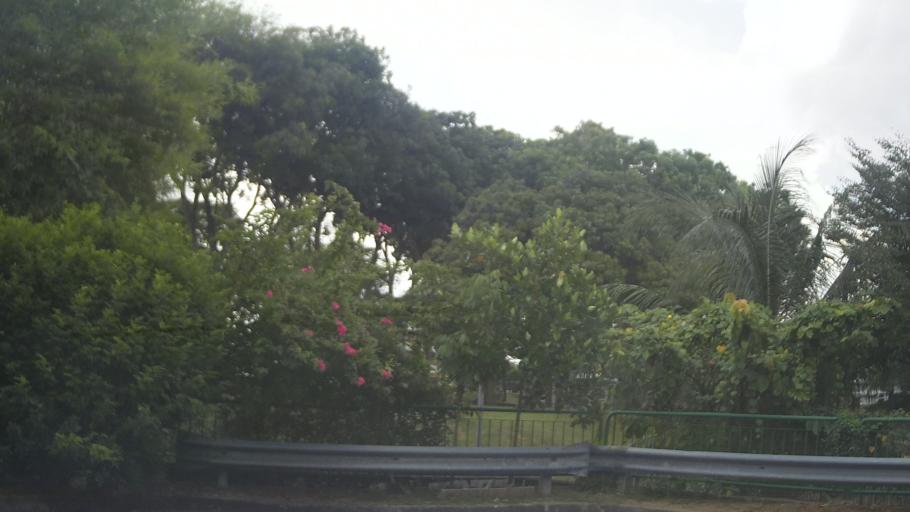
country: MY
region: Johor
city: Kampung Pasir Gudang Baru
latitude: 1.3871
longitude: 103.8556
